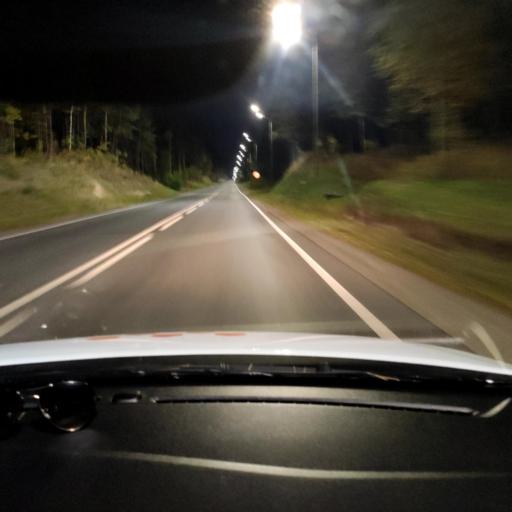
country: RU
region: Tatarstan
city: Verkhniy Uslon
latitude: 55.6377
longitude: 49.0490
